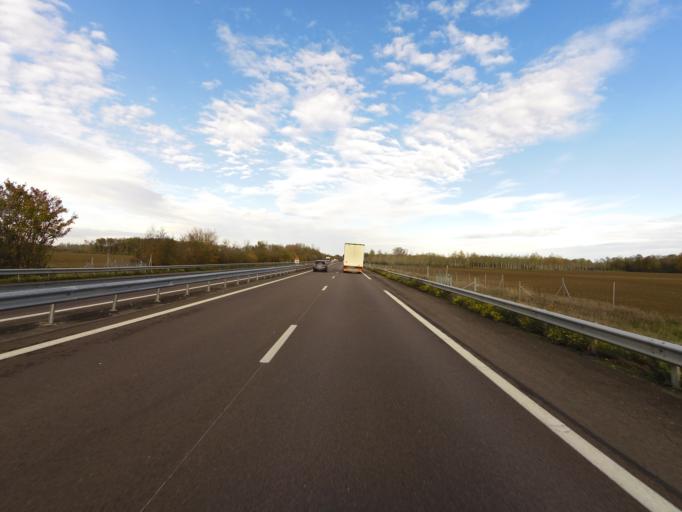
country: FR
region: Bourgogne
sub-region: Departement de la Cote-d'Or
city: Neuilly-les-Dijon
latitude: 47.2559
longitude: 5.1190
